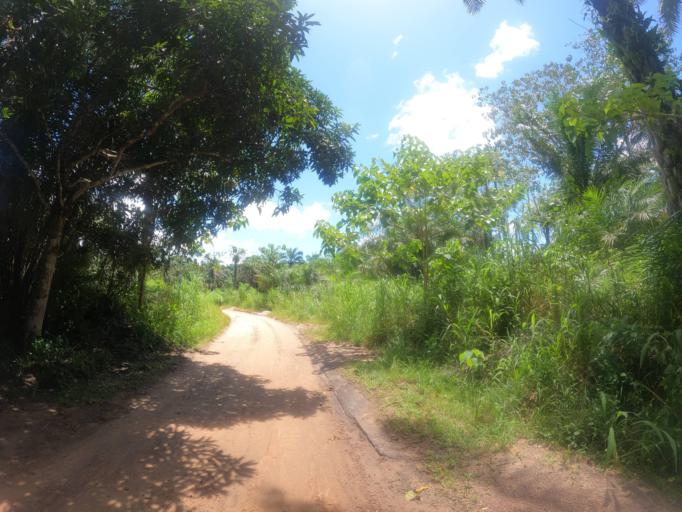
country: SL
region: Northern Province
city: Makeni
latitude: 8.8535
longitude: -12.1156
